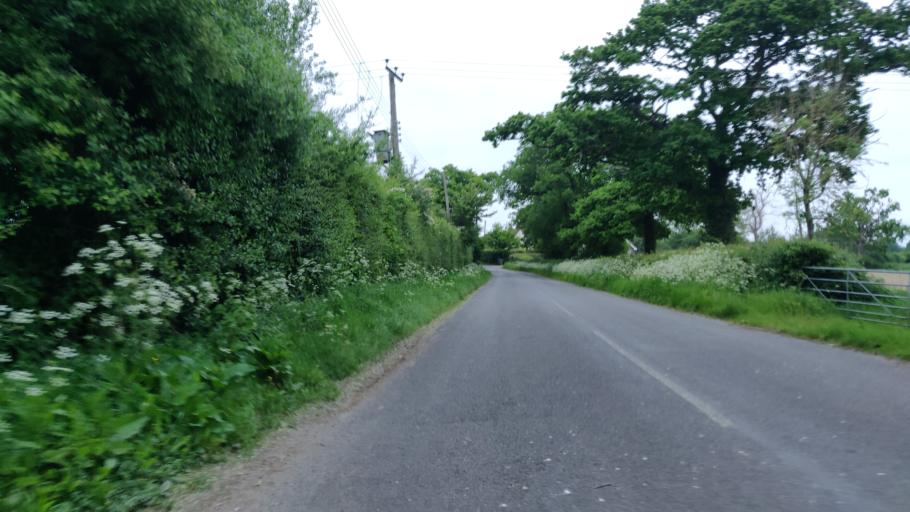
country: GB
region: England
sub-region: West Sussex
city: Partridge Green
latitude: 50.9958
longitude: -0.3029
